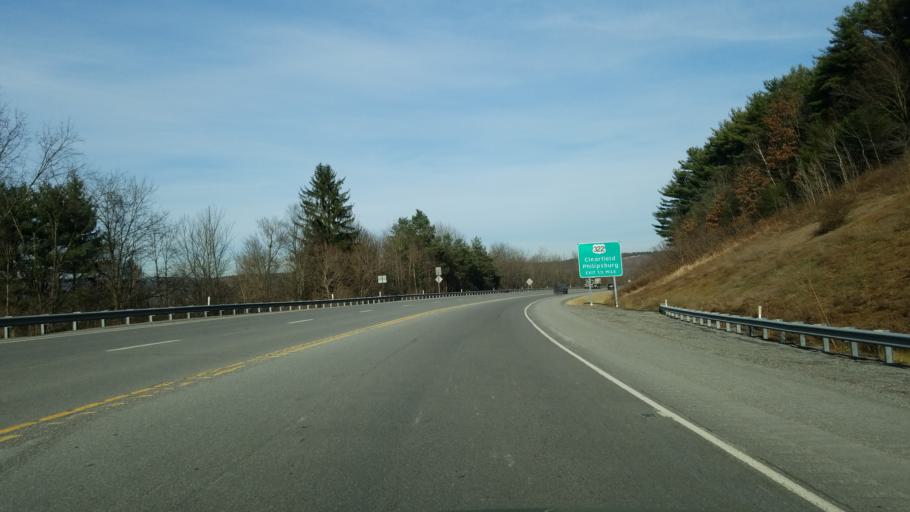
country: US
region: Pennsylvania
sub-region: Clearfield County
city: Clearfield
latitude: 41.0179
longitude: -78.4279
